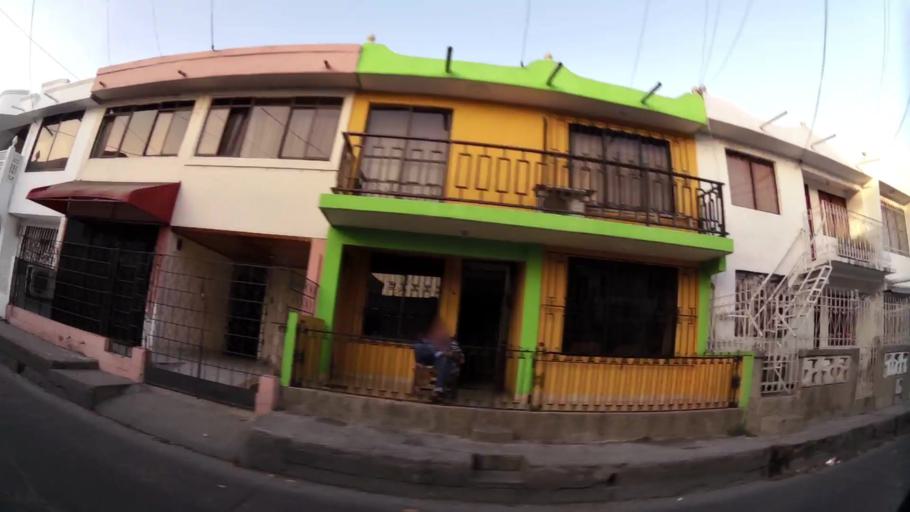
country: CO
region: Bolivar
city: Cartagena
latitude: 10.3914
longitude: -75.4852
